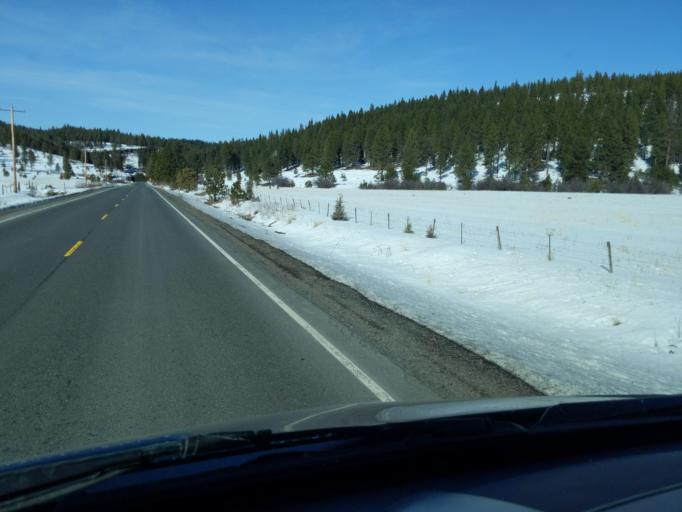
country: US
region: Oregon
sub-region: Grant County
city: John Day
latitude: 44.9275
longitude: -119.0102
